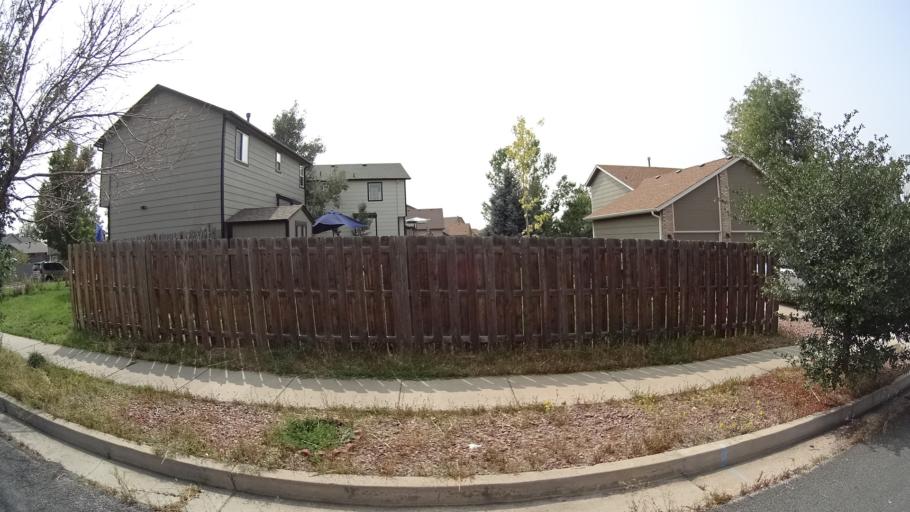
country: US
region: Colorado
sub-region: El Paso County
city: Cimarron Hills
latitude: 38.9252
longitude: -104.7265
